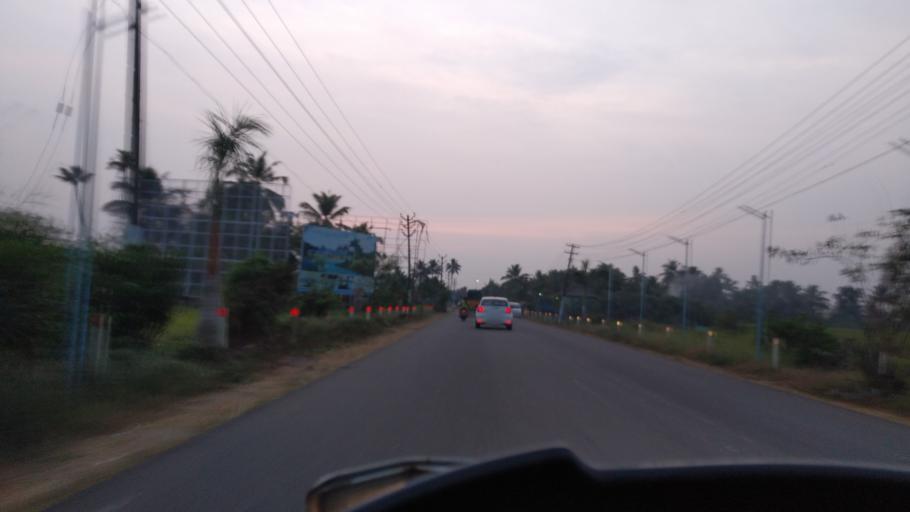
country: IN
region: Kerala
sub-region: Kottayam
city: Kottayam
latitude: 9.5923
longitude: 76.4534
